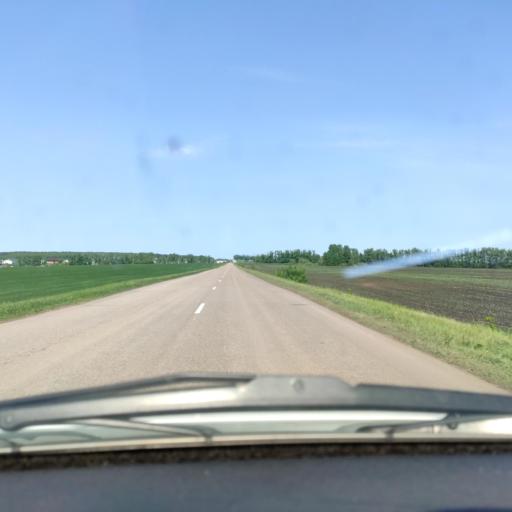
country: RU
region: Bashkortostan
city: Avdon
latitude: 54.5441
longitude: 55.6499
